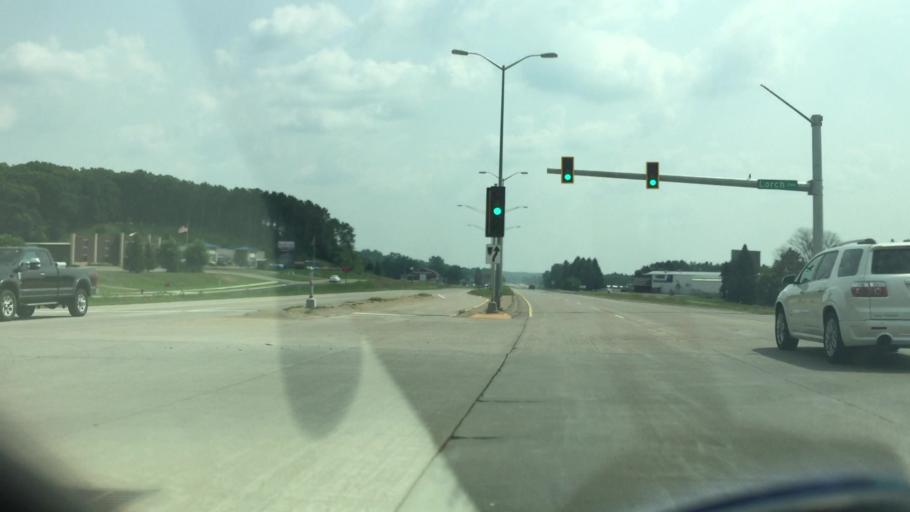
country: US
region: Wisconsin
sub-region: Eau Claire County
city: Altoona
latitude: 44.7617
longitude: -91.4585
